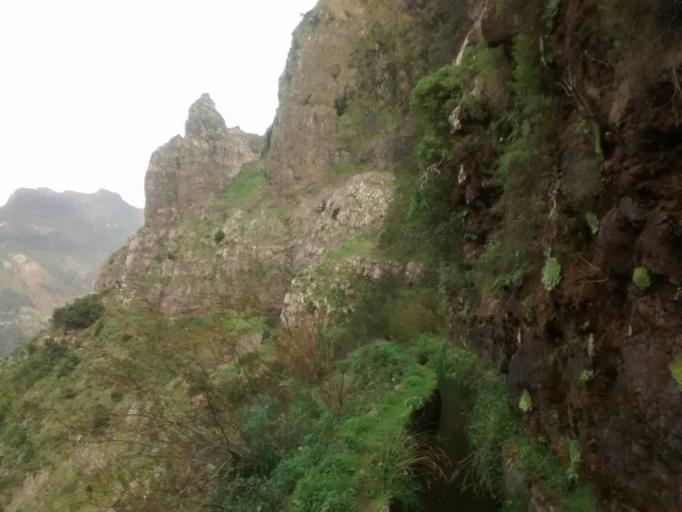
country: PT
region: Madeira
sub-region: Ribeira Brava
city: Campanario
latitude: 32.7187
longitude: -17.0261
